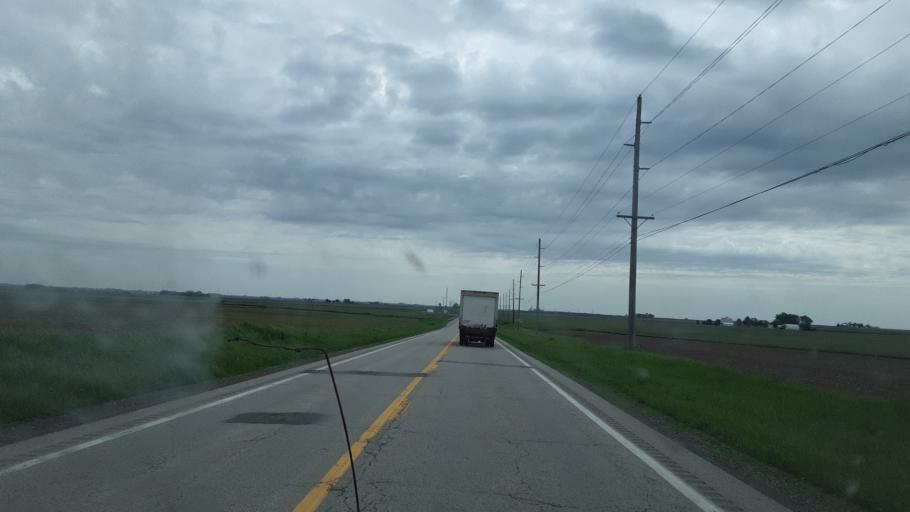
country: US
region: Illinois
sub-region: Tazewell County
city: Delavan
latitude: 40.3058
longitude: -89.5779
